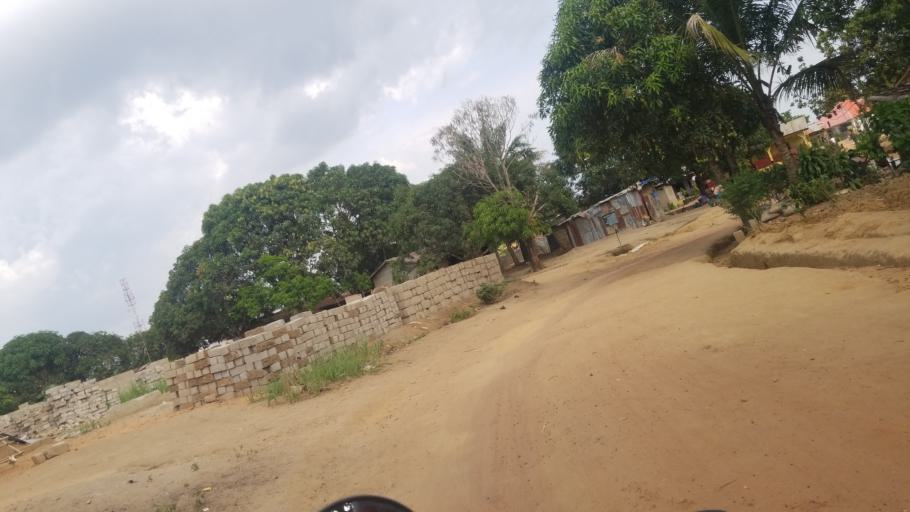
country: SL
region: Western Area
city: Waterloo
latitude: 8.3189
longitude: -13.0497
